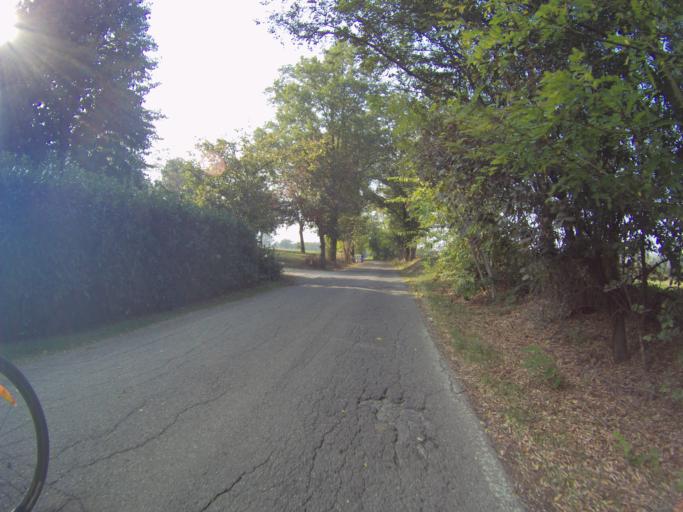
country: IT
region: Emilia-Romagna
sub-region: Provincia di Reggio Emilia
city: San Bartolomeo
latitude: 44.6554
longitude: 10.5563
